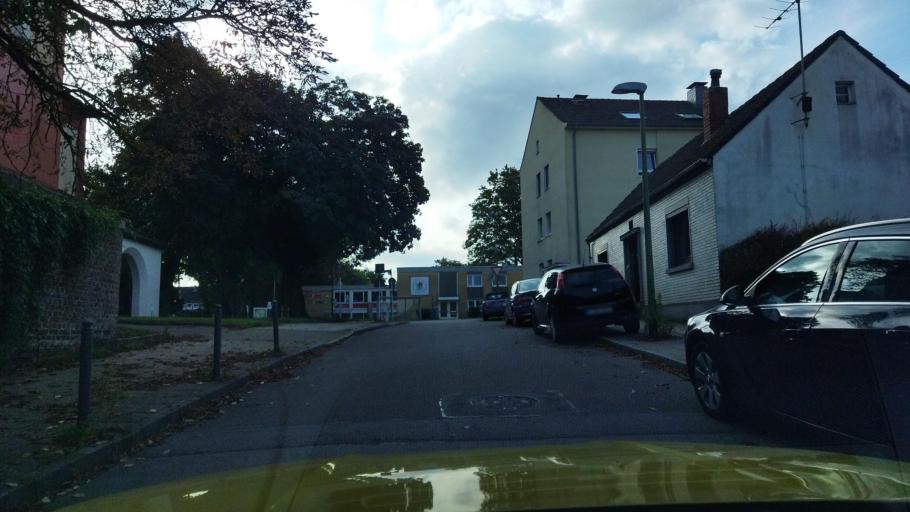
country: DE
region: North Rhine-Westphalia
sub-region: Regierungsbezirk Munster
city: Bottrop
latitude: 51.4659
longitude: 6.9507
